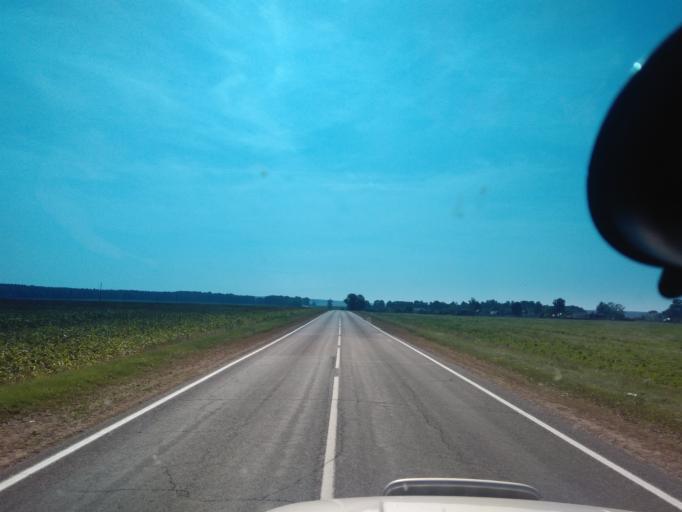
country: BY
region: Minsk
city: Uzda
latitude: 53.4164
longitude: 27.2144
